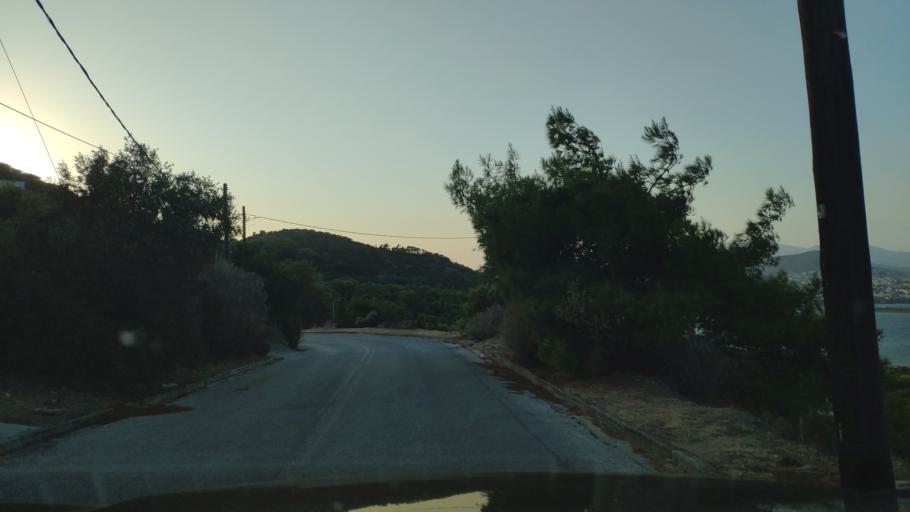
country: GR
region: Attica
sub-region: Nomarchia Anatolikis Attikis
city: Limin Mesoyaias
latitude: 37.9165
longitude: 24.0217
